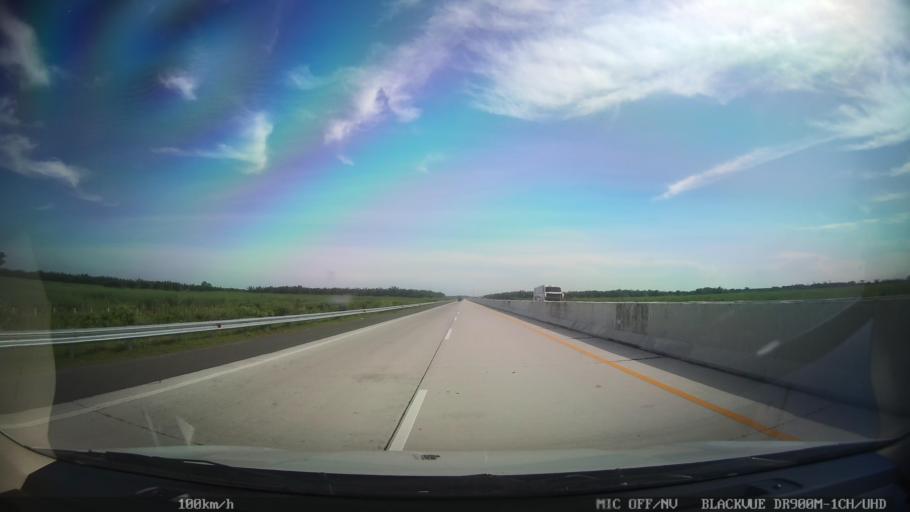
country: ID
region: North Sumatra
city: Binjai
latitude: 3.6826
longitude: 98.5376
